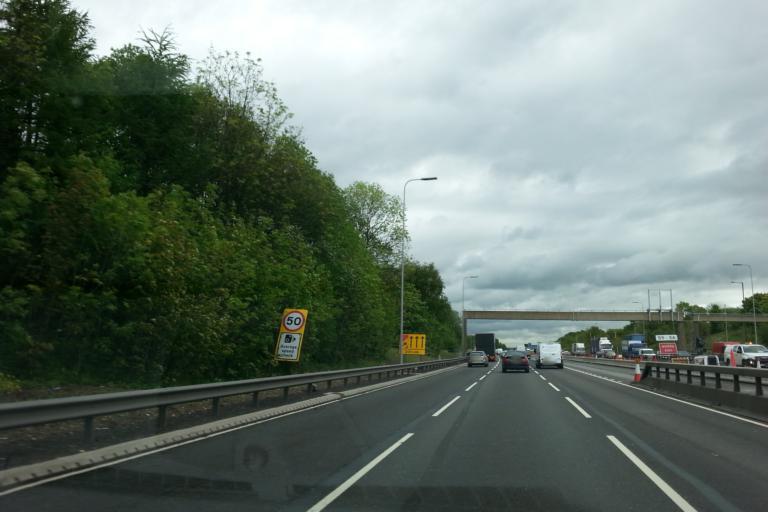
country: GB
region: England
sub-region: Manchester
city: Heywood
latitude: 53.5770
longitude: -2.2057
